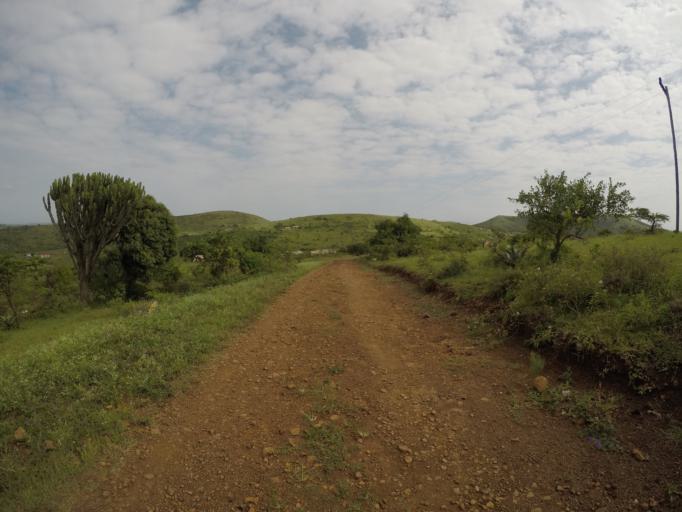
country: ZA
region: KwaZulu-Natal
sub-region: uThungulu District Municipality
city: Empangeni
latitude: -28.6248
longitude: 31.9009
